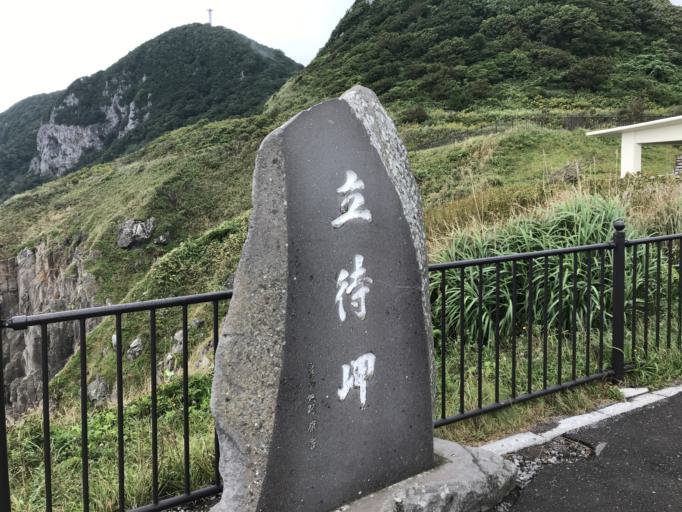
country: JP
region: Hokkaido
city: Hakodate
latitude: 41.7453
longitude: 140.7209
